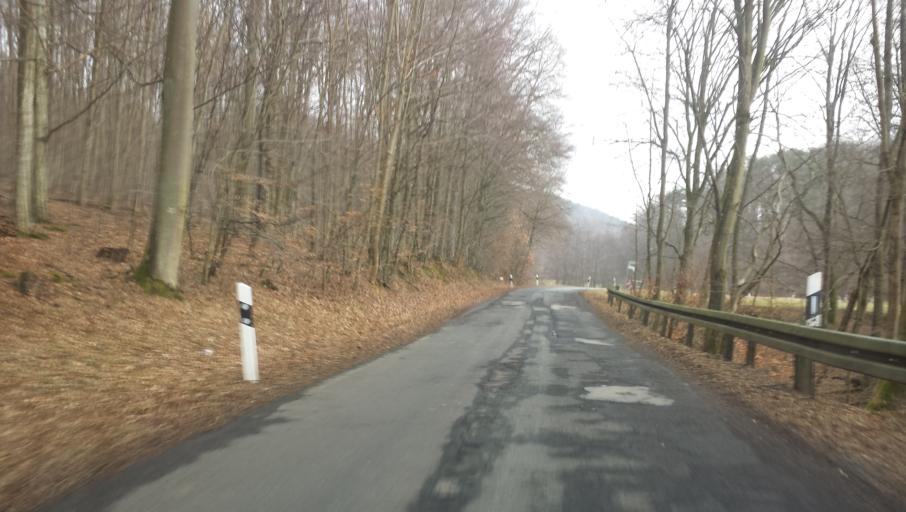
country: DE
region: Hesse
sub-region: Regierungsbezirk Darmstadt
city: Brensbach
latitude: 49.8029
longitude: 8.9113
